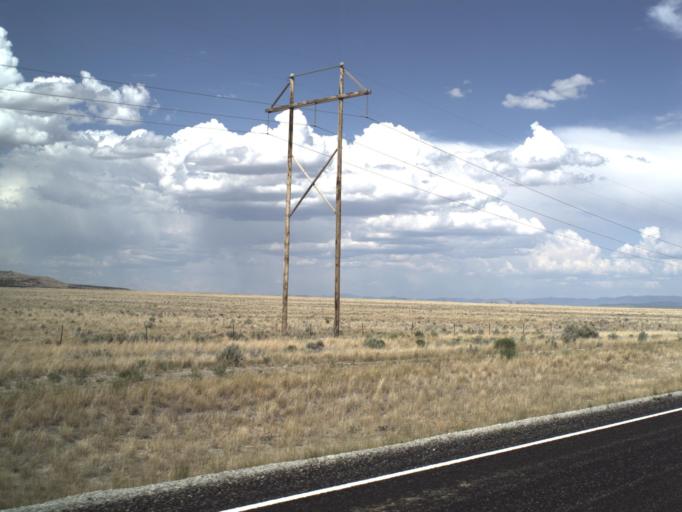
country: US
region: Idaho
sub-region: Power County
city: American Falls
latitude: 41.9695
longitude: -113.1131
